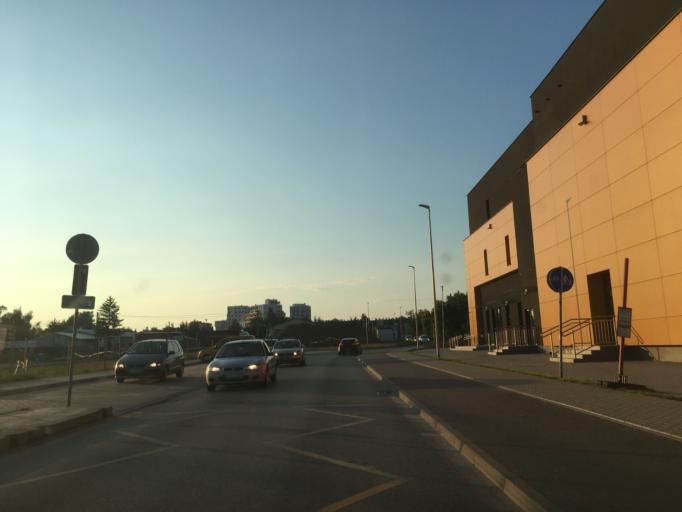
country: PL
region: Masovian Voivodeship
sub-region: Powiat piaseczynski
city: Piaseczno
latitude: 52.0731
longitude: 21.0128
